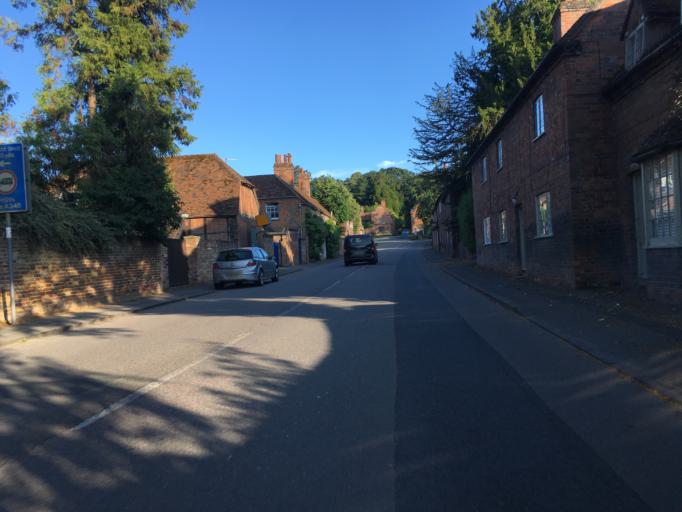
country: GB
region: England
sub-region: Hampshire
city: Tadley
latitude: 51.3831
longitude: -1.1527
